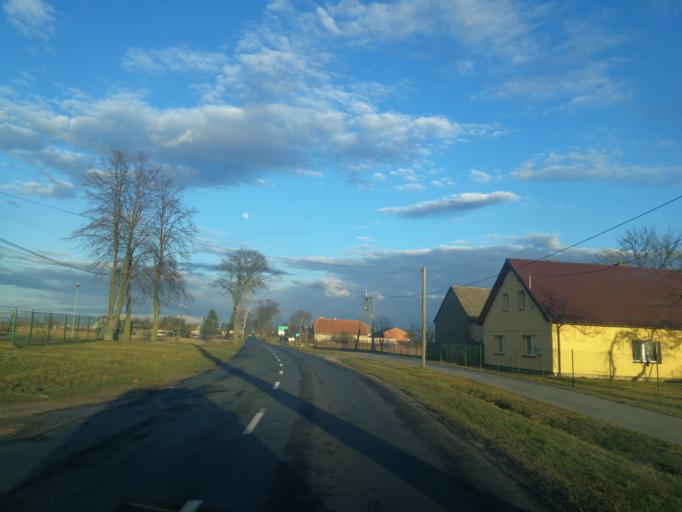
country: PL
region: Kujawsko-Pomorskie
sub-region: Powiat torunski
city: Chelmza
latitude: 53.1880
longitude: 18.6301
